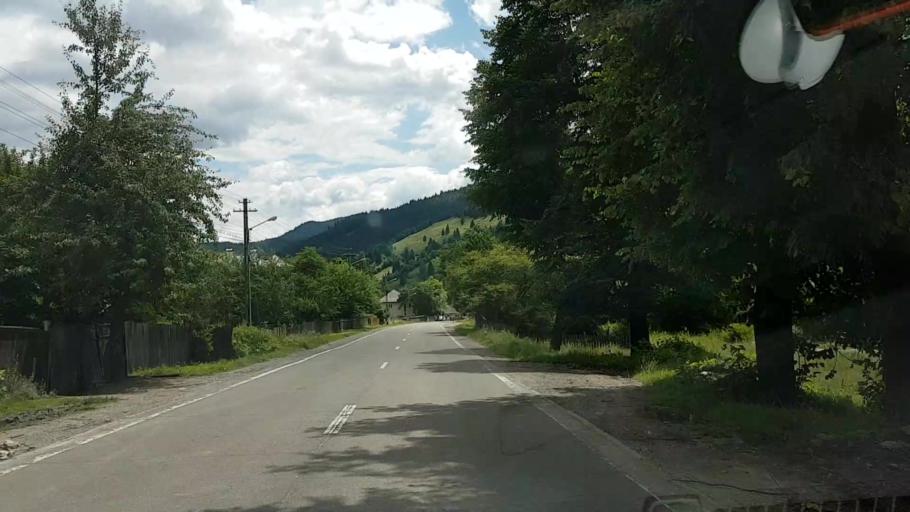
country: RO
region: Suceava
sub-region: Comuna Brosteni
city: Brosteni
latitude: 47.2387
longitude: 25.7097
